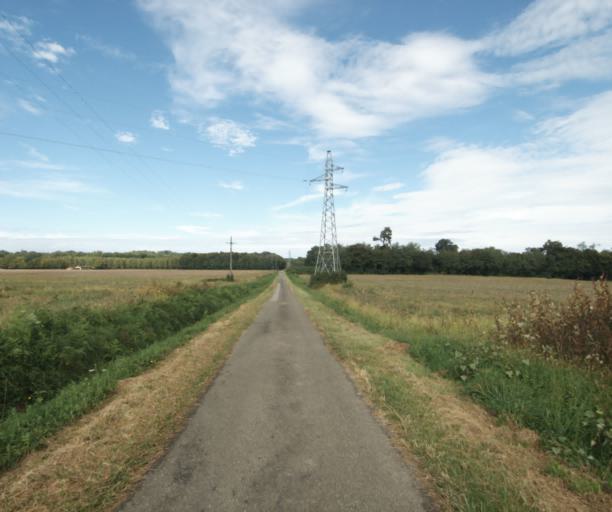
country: FR
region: Aquitaine
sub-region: Departement des Landes
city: Villeneuve-de-Marsan
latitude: 43.9029
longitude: -0.2254
